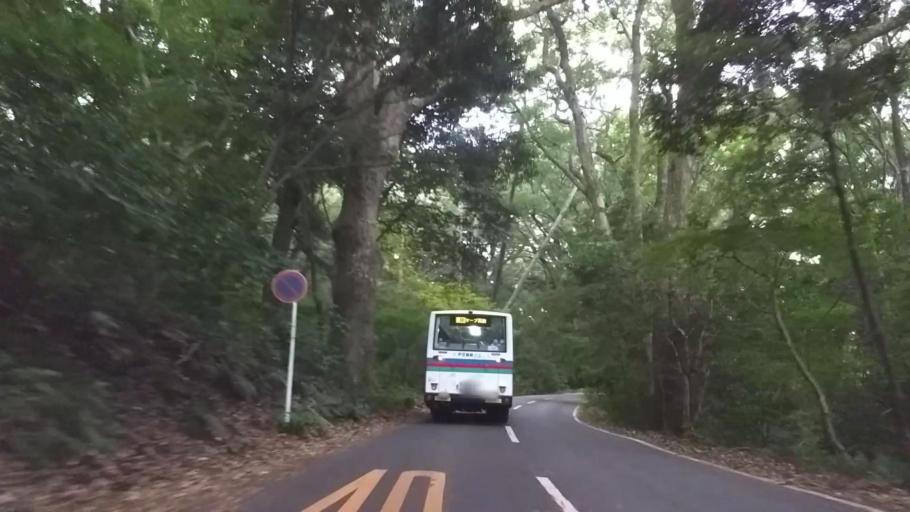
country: JP
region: Kanagawa
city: Yugawara
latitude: 35.1460
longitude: 139.1548
